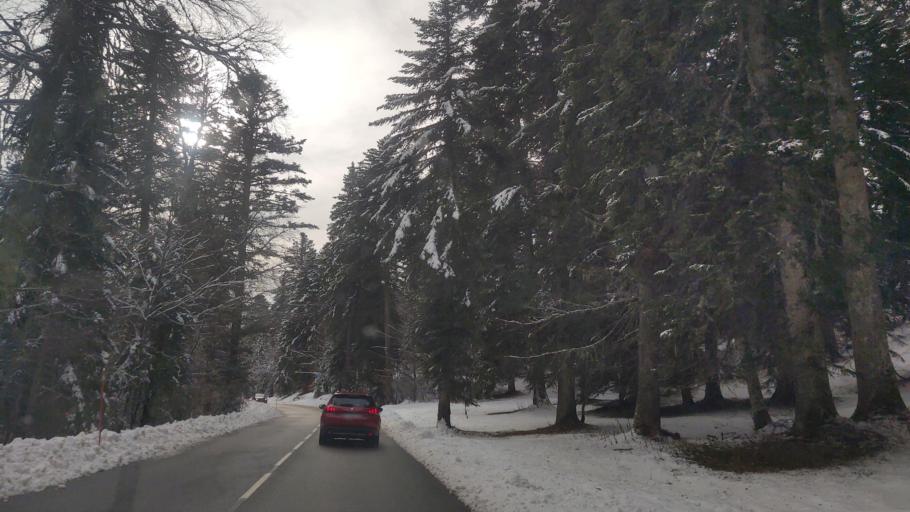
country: FR
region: Rhone-Alpes
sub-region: Departement de la Savoie
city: Mery
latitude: 45.6582
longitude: 5.9793
